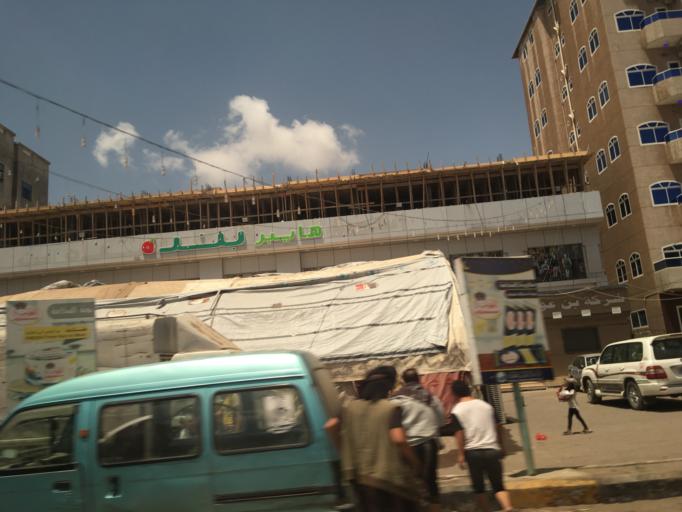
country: YE
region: Aden
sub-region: Al Mansura
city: Al Mansurah
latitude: 12.8603
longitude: 44.9722
